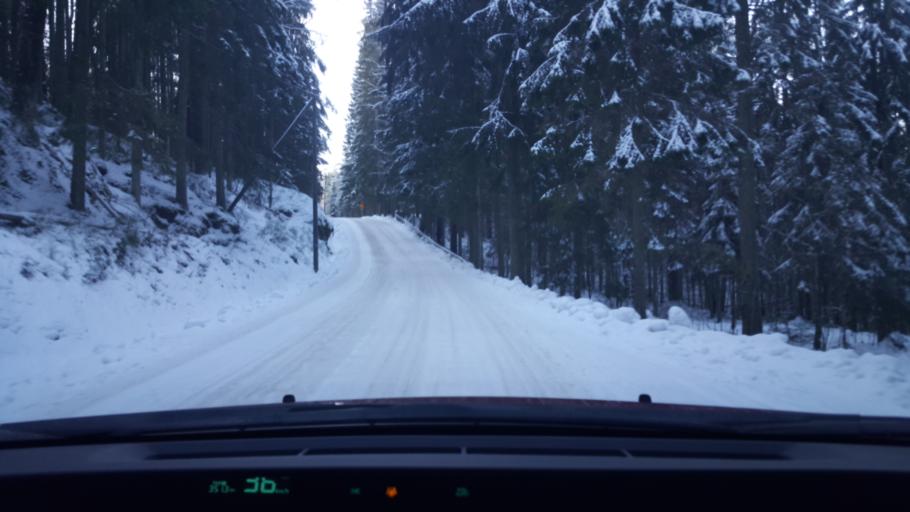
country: FI
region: Uusimaa
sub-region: Helsinki
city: Espoo
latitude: 60.3098
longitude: 24.5254
